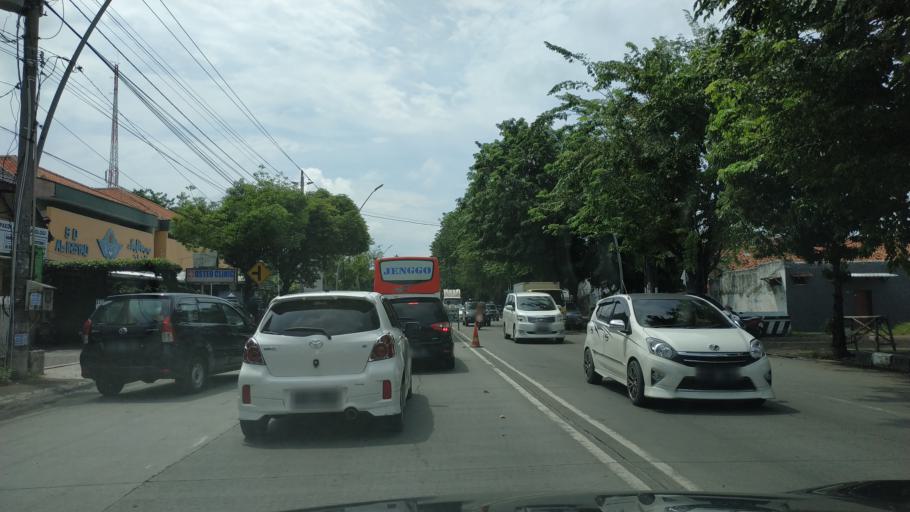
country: ID
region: Central Java
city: Tegal
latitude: -6.8680
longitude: 109.1333
